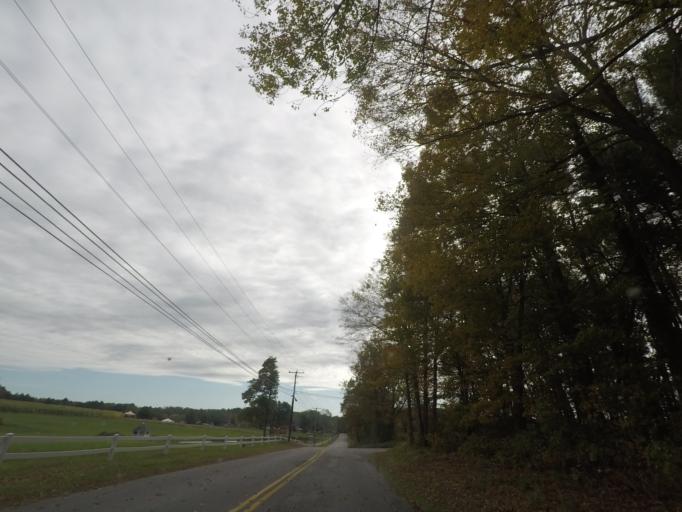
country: US
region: Connecticut
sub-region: Windham County
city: Thompson
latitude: 41.9516
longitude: -71.8460
